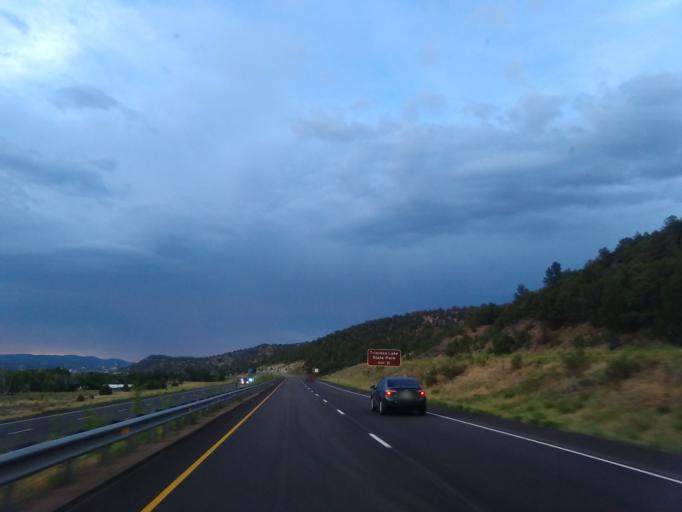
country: US
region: Colorado
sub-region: Las Animas County
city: Trinidad
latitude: 37.1084
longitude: -104.5232
